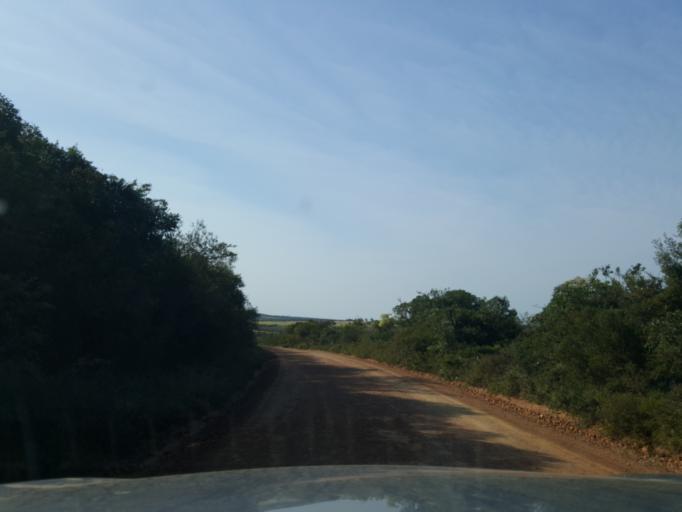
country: ZA
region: Eastern Cape
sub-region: Cacadu District Municipality
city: Grahamstown
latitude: -33.4100
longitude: 26.3020
